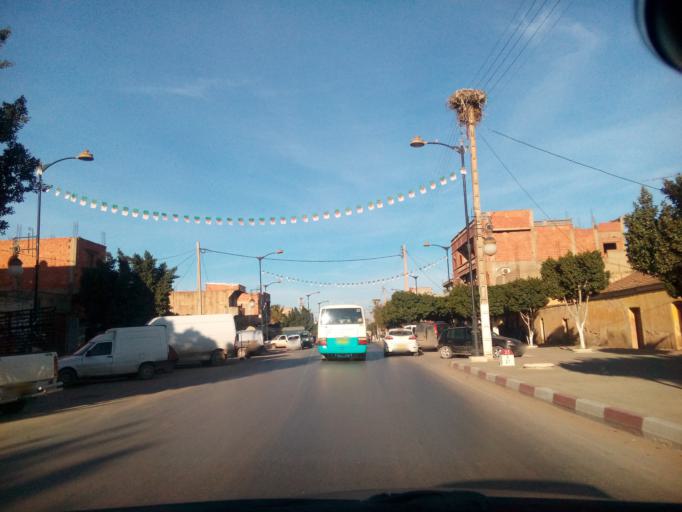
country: DZ
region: Mostaganem
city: Mostaganem
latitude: 35.7788
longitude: 0.1911
